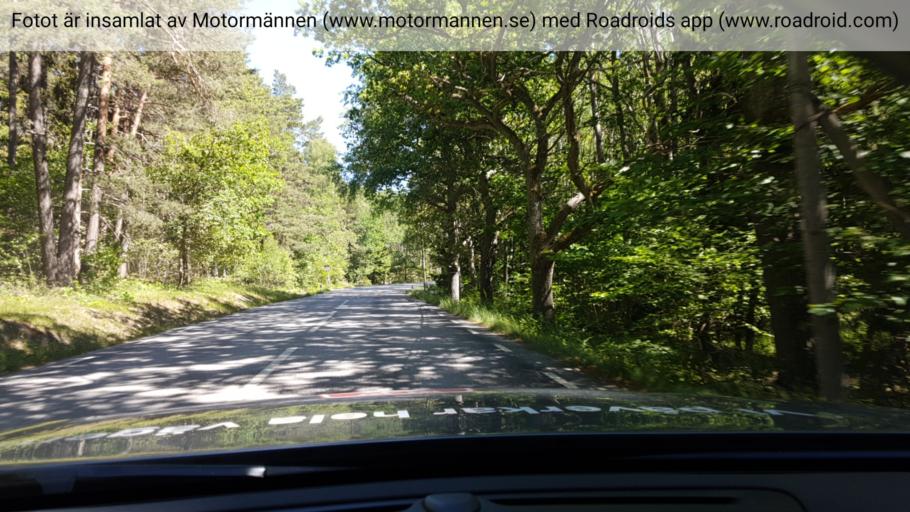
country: SE
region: Stockholm
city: Dalaro
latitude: 59.1234
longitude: 18.3082
